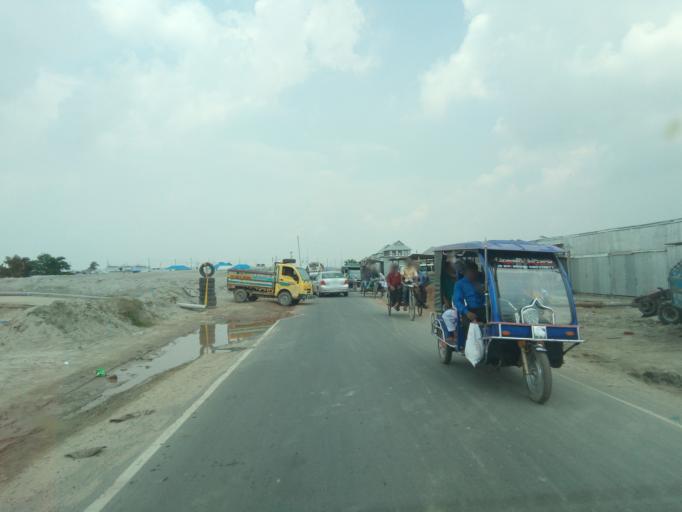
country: BD
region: Dhaka
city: Char Bhadrasan
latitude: 23.4164
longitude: 90.2182
